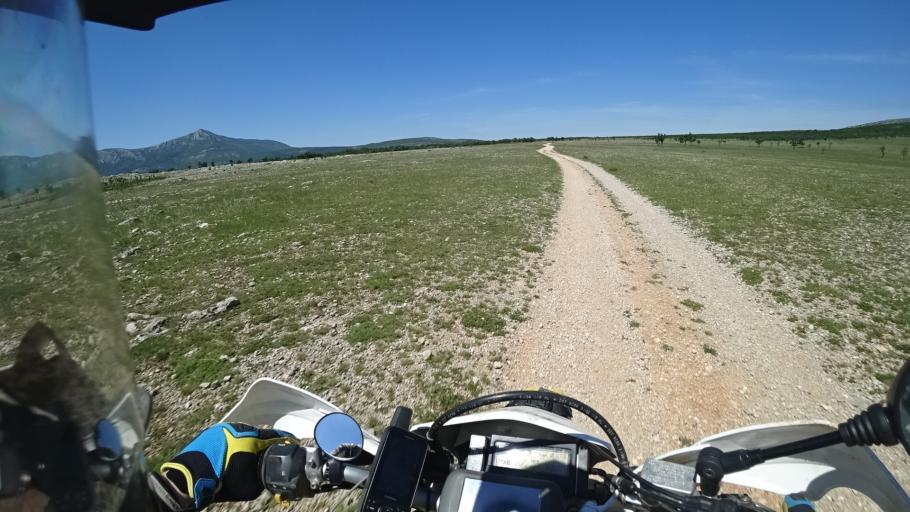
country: BA
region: Federation of Bosnia and Herzegovina
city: Bosansko Grahovo
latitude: 44.0041
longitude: 16.3972
